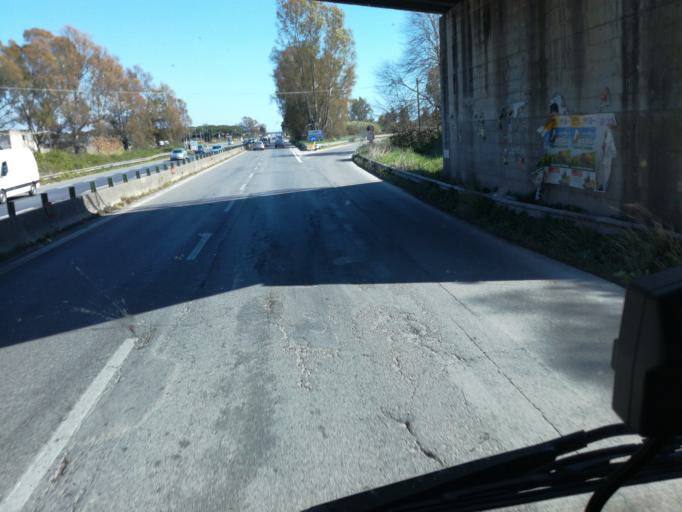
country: IT
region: Latium
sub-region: Provincia di Latina
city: Aprilia
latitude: 41.5688
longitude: 12.6694
